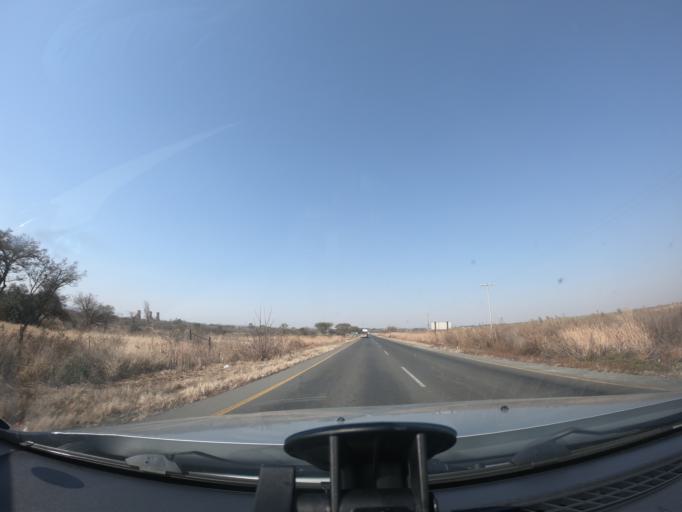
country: ZA
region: KwaZulu-Natal
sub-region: uThukela District Municipality
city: Ladysmith
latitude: -28.7299
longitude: 29.8108
